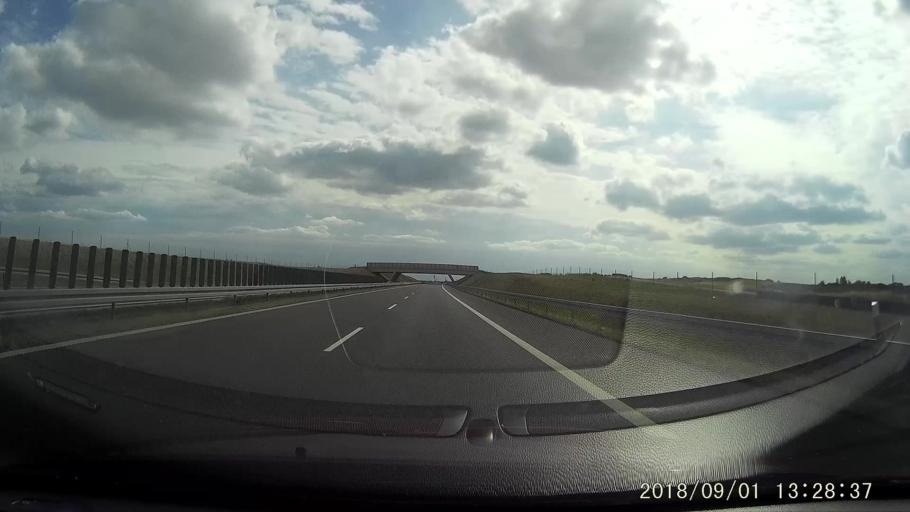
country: PL
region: West Pomeranian Voivodeship
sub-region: Powiat pyrzycki
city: Kozielice
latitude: 53.0704
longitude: 14.8605
